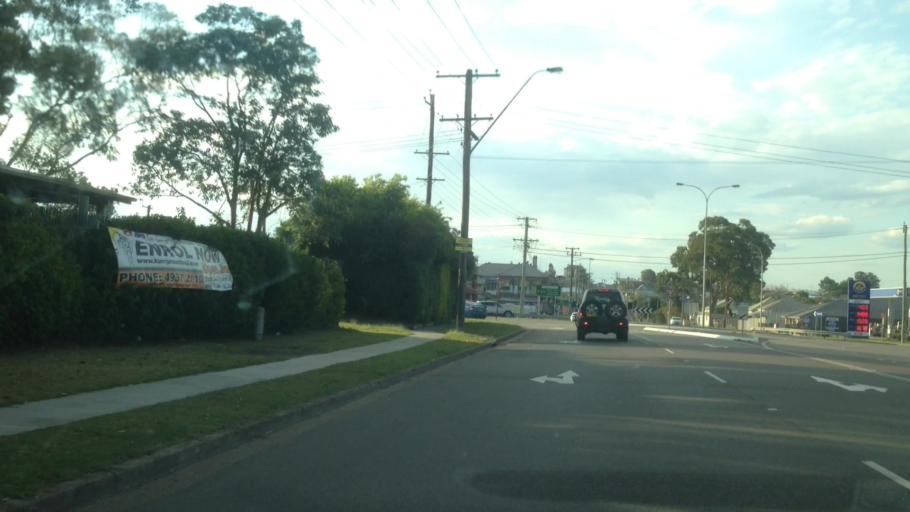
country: AU
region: New South Wales
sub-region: Cessnock
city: Kurri Kurri
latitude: -32.8250
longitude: 151.4866
